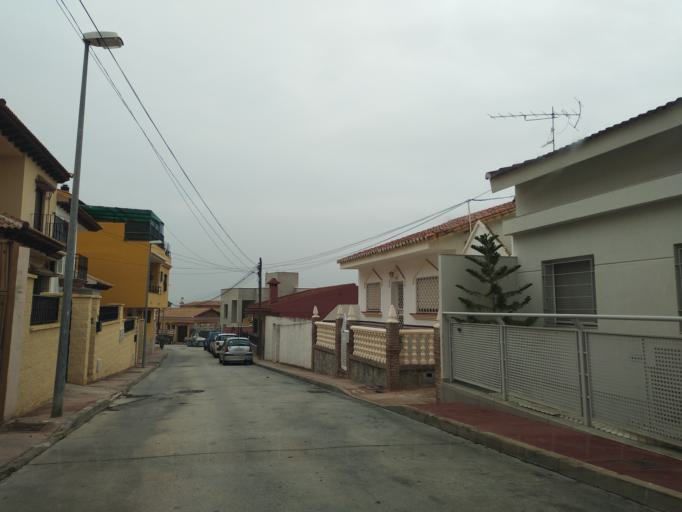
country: ES
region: Andalusia
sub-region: Provincia de Malaga
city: Malaga
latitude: 36.7466
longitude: -4.4773
